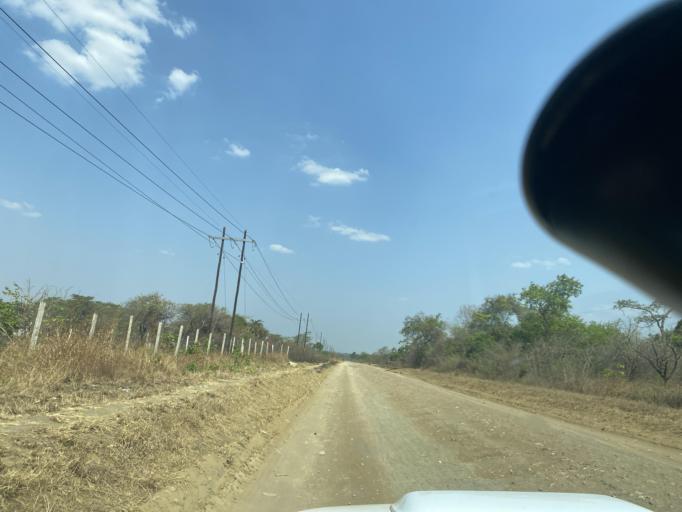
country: ZM
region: Lusaka
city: Lusaka
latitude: -15.3131
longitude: 28.0533
